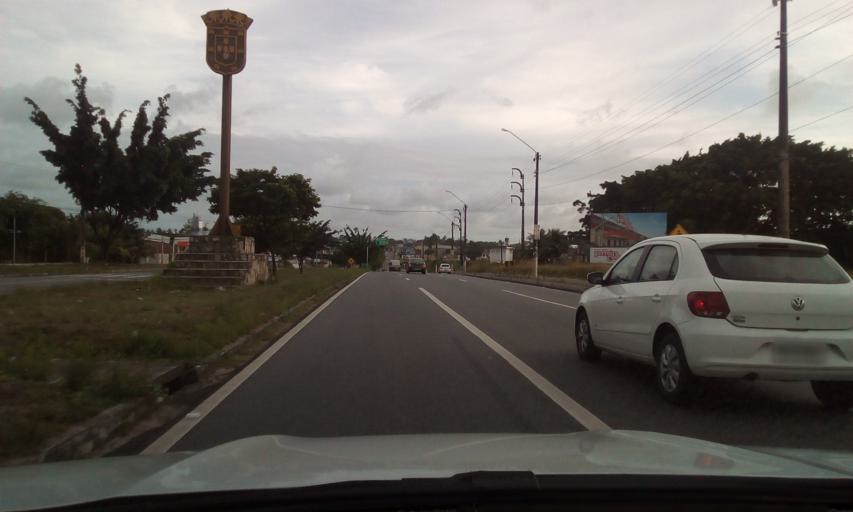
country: BR
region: Pernambuco
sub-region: Igarassu
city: Igarassu
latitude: -7.8420
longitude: -34.9114
